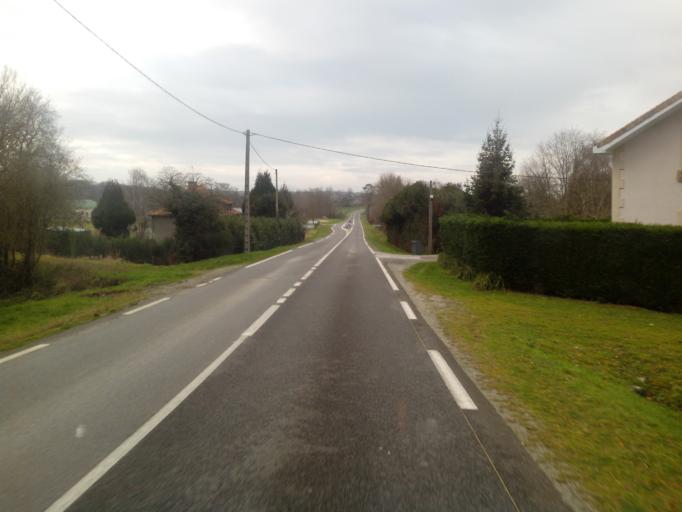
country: FR
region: Limousin
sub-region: Departement de la Haute-Vienne
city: Magnac-Laval
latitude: 46.2144
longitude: 1.1546
